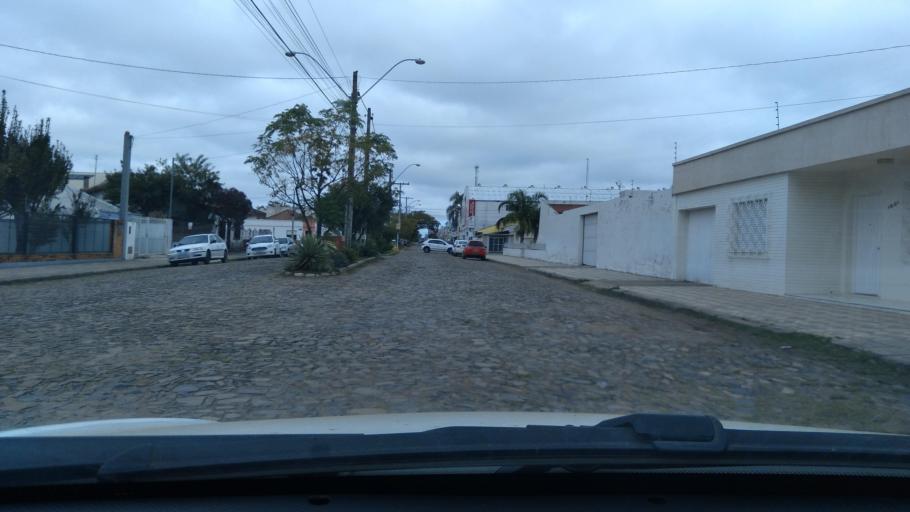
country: BR
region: Rio Grande do Sul
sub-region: Dom Pedrito
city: Dom Pedrito
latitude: -30.9775
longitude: -54.6709
